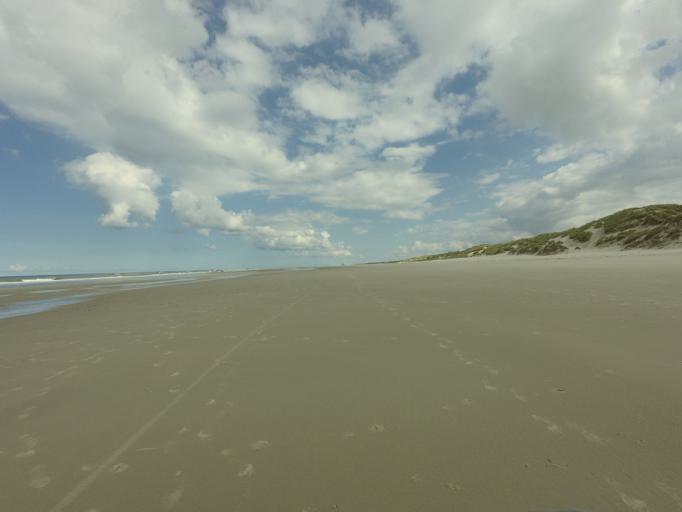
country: NL
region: Friesland
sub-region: Gemeente Terschelling
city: West-Terschelling
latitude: 53.4004
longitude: 5.2335
